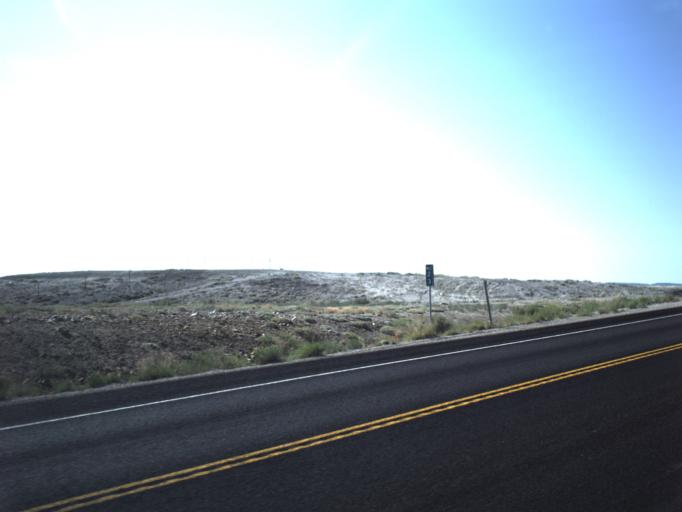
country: US
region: Utah
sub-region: Emery County
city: Ferron
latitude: 39.0367
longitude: -111.1278
